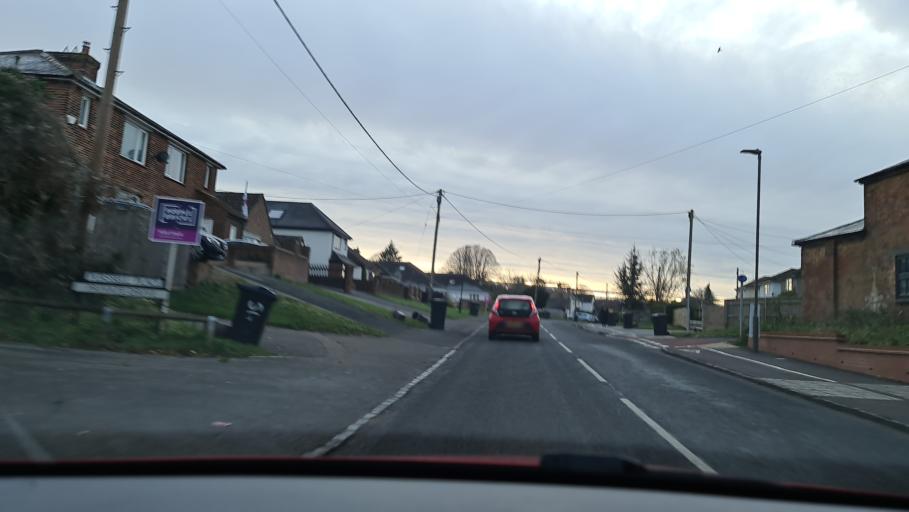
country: GB
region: England
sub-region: Buckinghamshire
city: Princes Risborough
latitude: 51.7289
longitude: -0.8351
